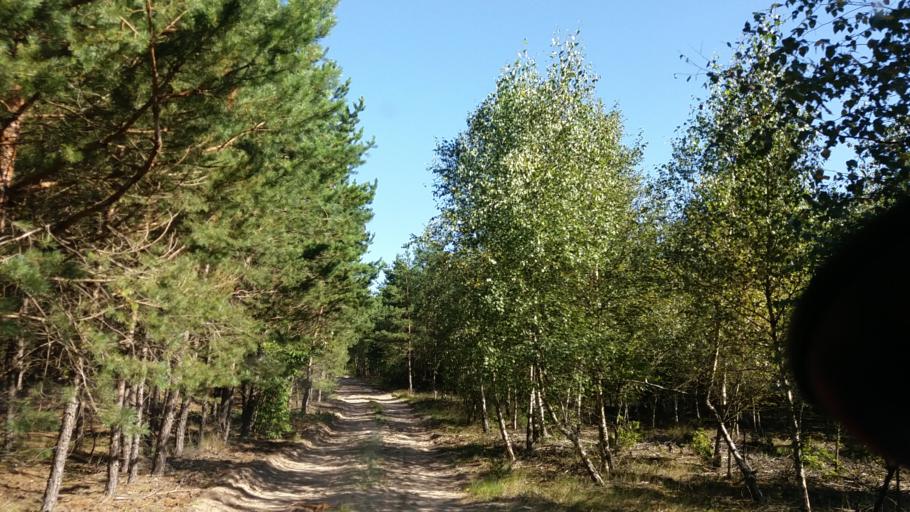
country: PL
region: West Pomeranian Voivodeship
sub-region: Powiat szczecinecki
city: Borne Sulinowo
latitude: 53.5796
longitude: 16.5099
